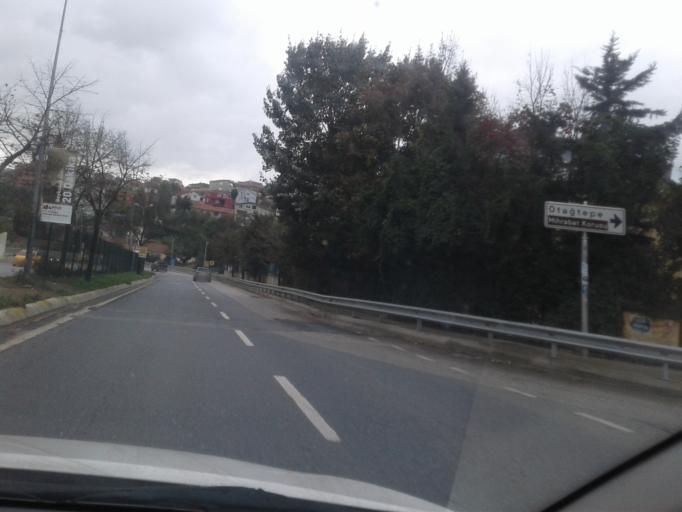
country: TR
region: Istanbul
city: Umraniye
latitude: 41.0883
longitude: 29.0863
